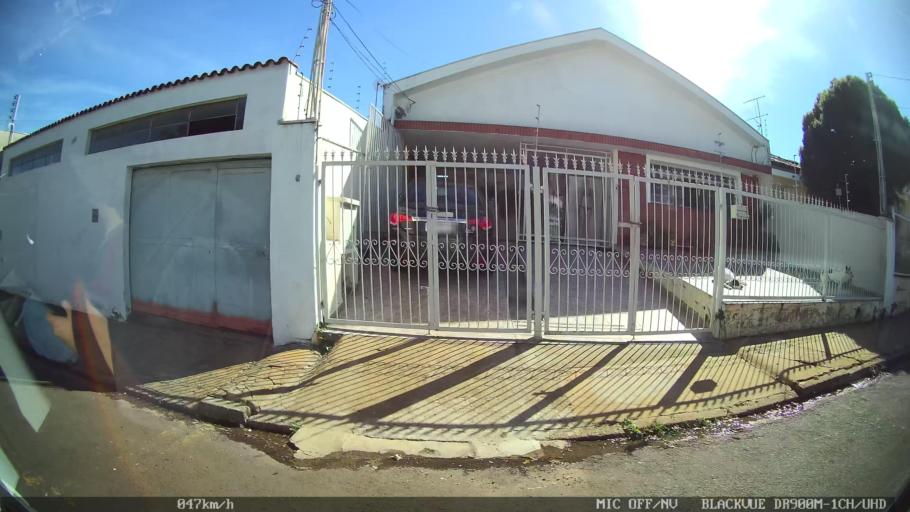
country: BR
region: Sao Paulo
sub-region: Franca
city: Franca
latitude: -20.5488
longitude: -47.3949
